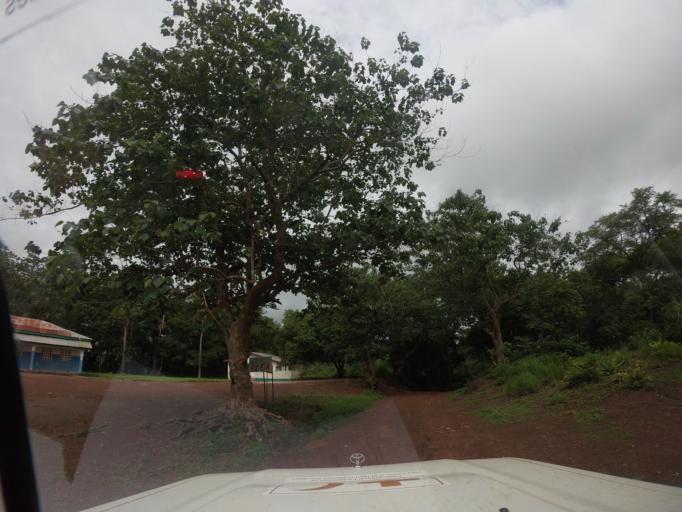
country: SL
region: Northern Province
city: Kamakwie
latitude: 9.6775
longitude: -12.2280
